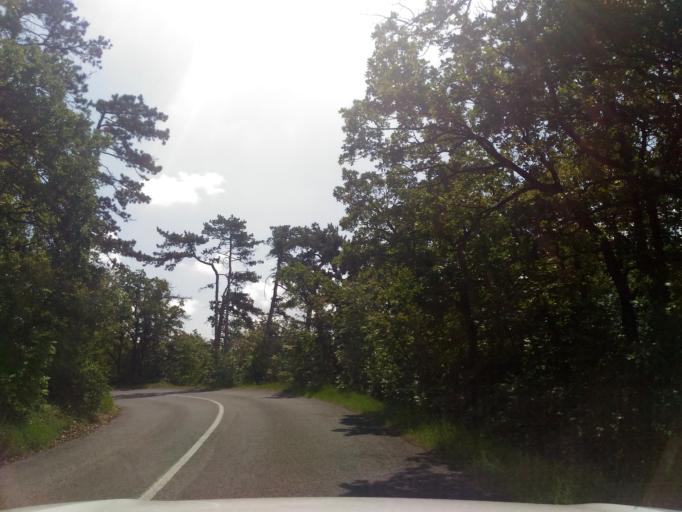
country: HU
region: Baranya
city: Pecs
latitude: 46.0904
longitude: 18.2232
